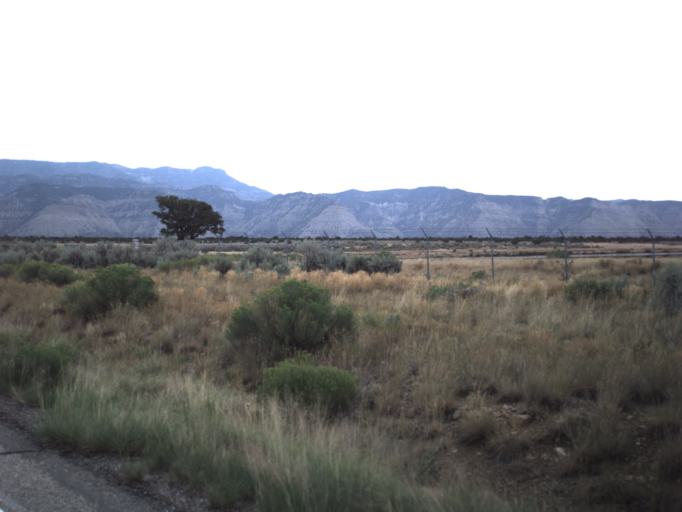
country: US
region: Utah
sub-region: Carbon County
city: East Carbon City
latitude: 39.5381
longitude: -110.4470
